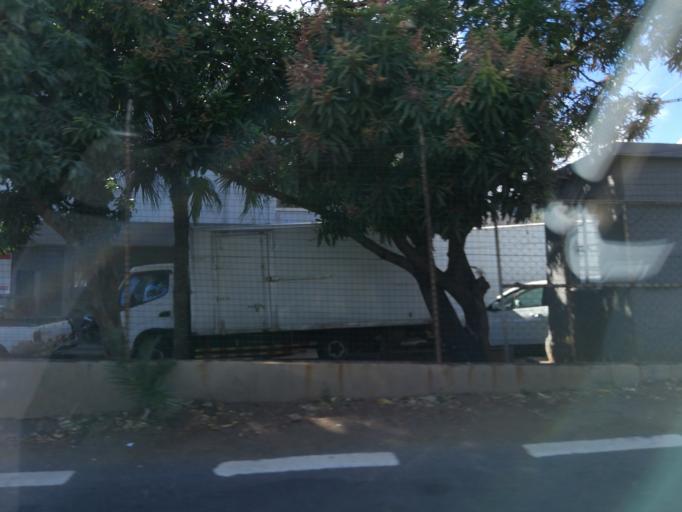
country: MU
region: Moka
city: Pailles
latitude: -20.1893
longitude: 57.4781
